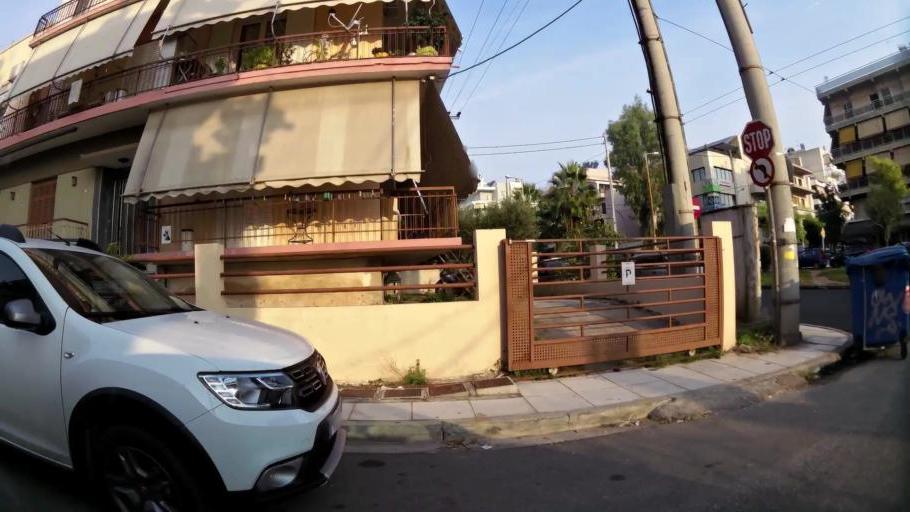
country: GR
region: Attica
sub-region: Nomarchia Athinas
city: Petroupolis
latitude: 38.0375
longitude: 23.6858
